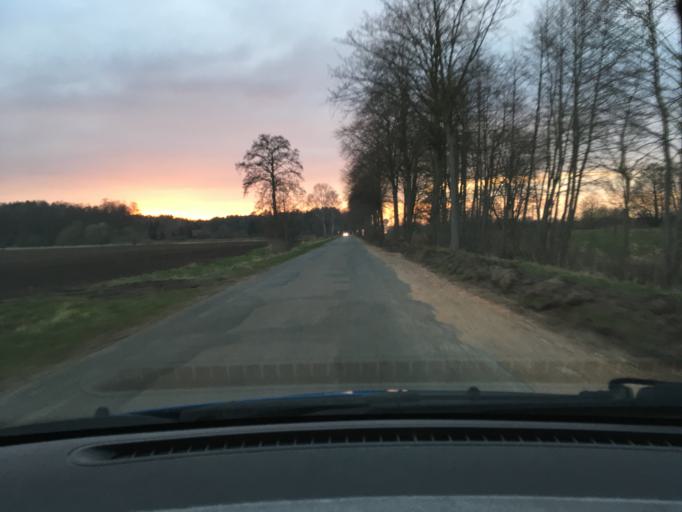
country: DE
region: Lower Saxony
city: Bleckede
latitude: 53.2906
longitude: 10.7097
